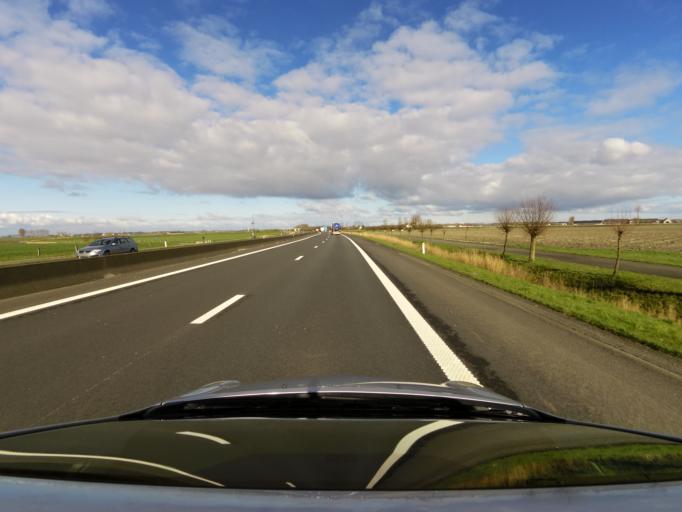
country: BE
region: Flanders
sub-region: Provincie West-Vlaanderen
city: Veurne
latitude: 51.0641
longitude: 2.6386
